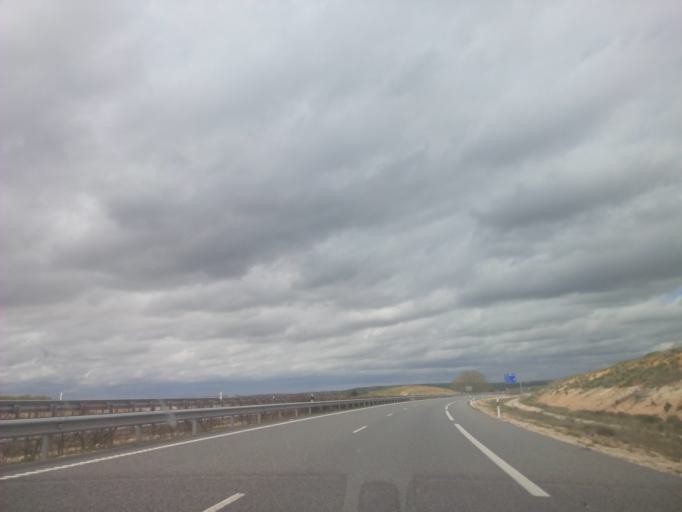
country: ES
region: Castille and Leon
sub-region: Provincia de Salamanca
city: Pelabravo
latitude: 40.9335
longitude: -5.5918
